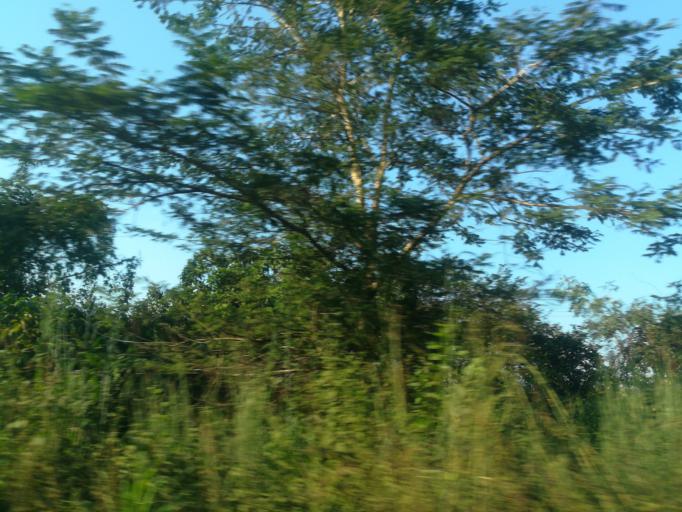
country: NG
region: Ogun
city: Abeokuta
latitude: 7.2132
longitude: 3.1927
